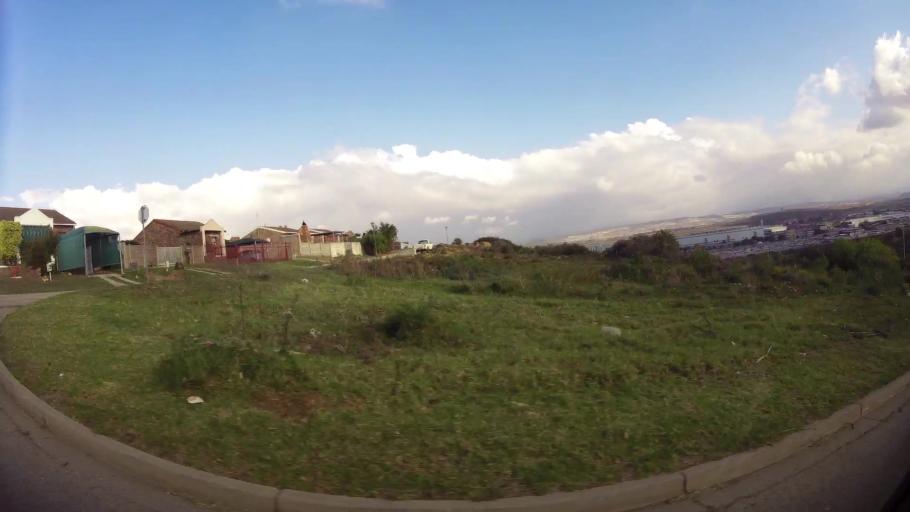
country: ZA
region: Eastern Cape
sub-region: Nelson Mandela Bay Metropolitan Municipality
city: Uitenhage
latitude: -33.7779
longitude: 25.4257
